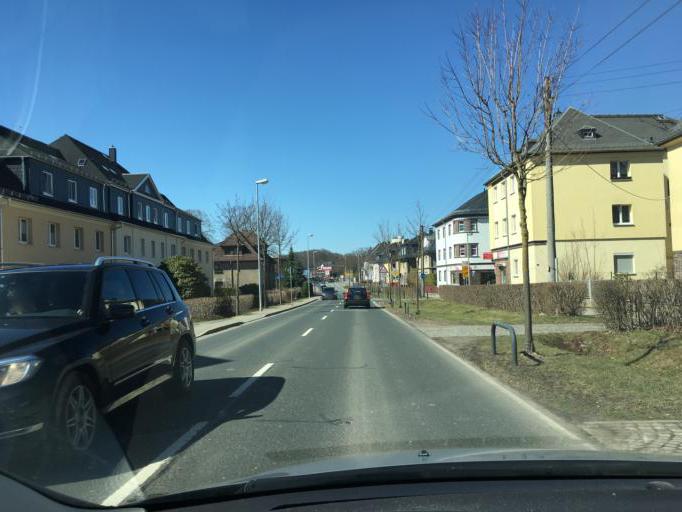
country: DE
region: Saxony
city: Neukirchen
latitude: 50.8240
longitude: 12.8354
